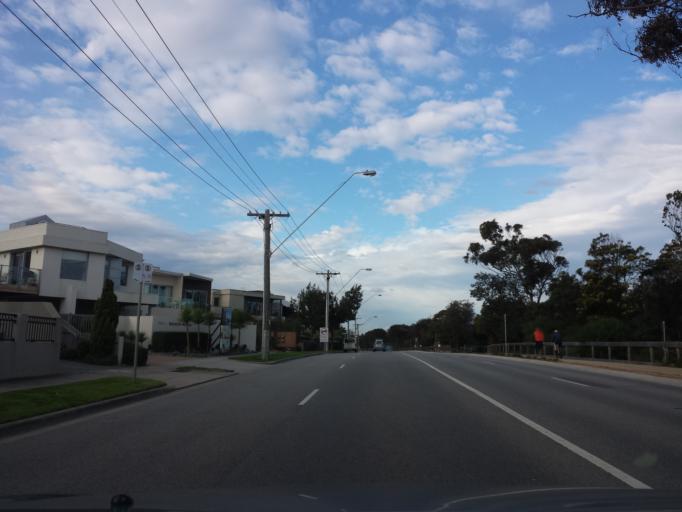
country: AU
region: Victoria
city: Beaumaris
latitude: -37.9895
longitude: 145.0448
